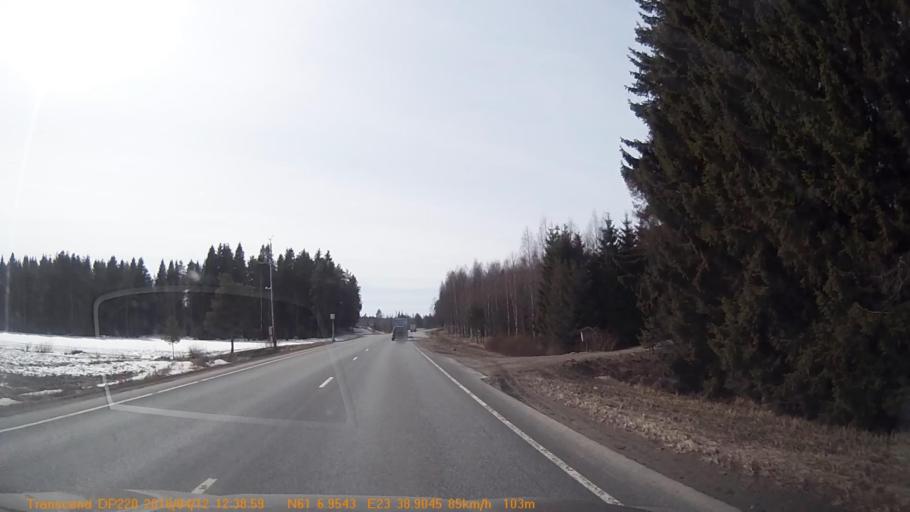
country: FI
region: Pirkanmaa
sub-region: Etelae-Pirkanmaa
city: Kylmaekoski
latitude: 61.1160
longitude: 23.6486
